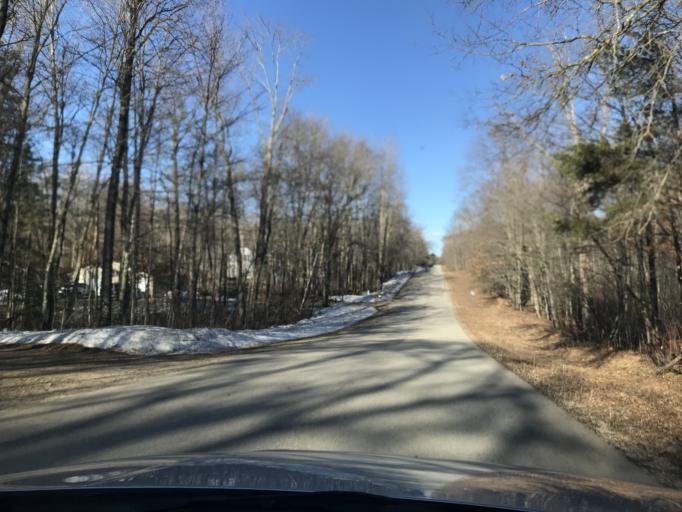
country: US
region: Wisconsin
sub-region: Marinette County
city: Niagara
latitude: 45.3903
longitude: -88.0704
